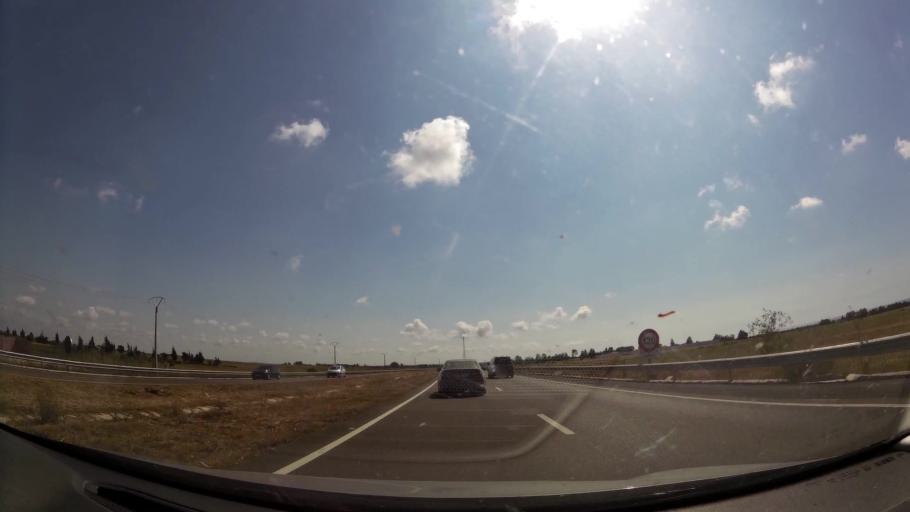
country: MA
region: Rabat-Sale-Zemmour-Zaer
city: Skhirat
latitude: 33.8630
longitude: -6.9662
